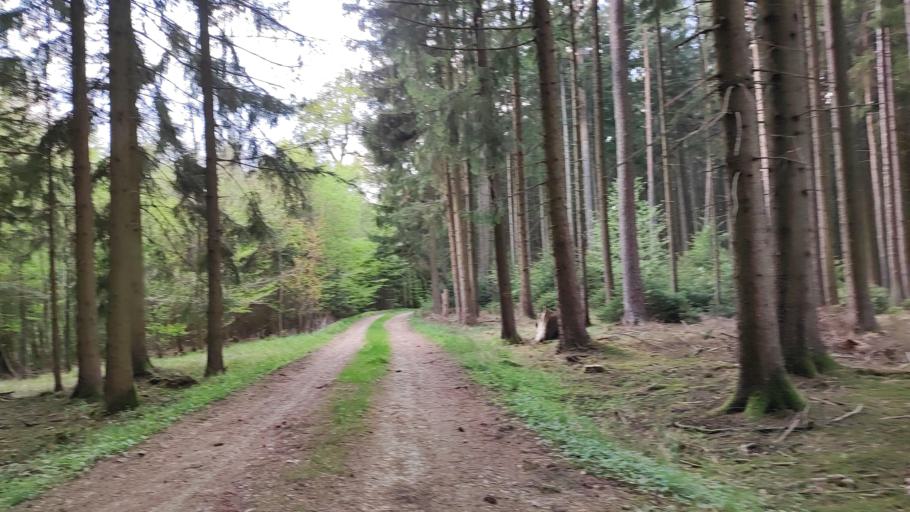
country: DE
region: Bavaria
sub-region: Swabia
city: Zusmarshausen
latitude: 48.4011
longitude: 10.6273
